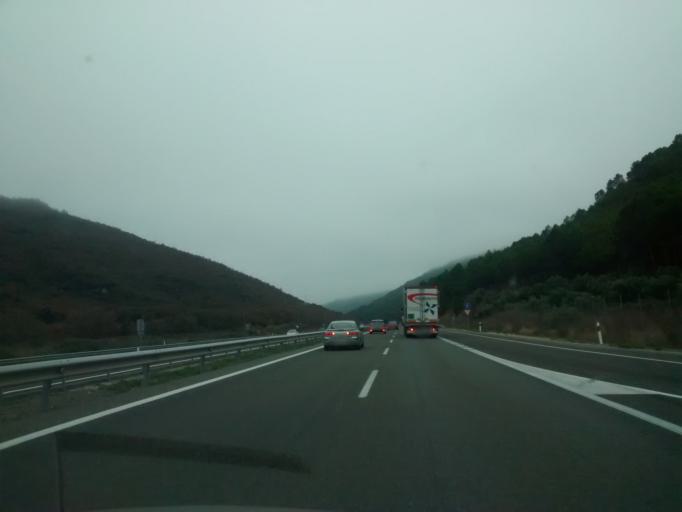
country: ES
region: Castille-La Mancha
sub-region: Provincia de Guadalajara
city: Ciruelas
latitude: 40.7187
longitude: -3.0627
